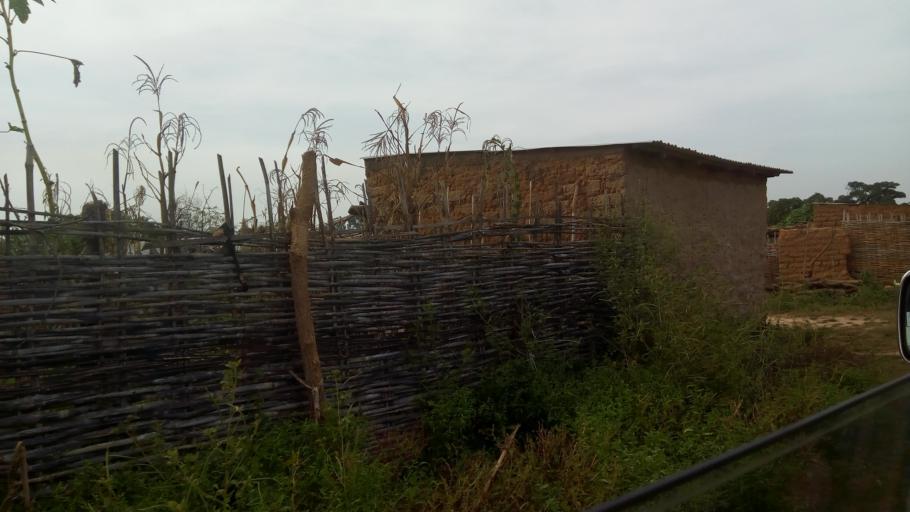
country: ML
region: Kayes
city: Kita
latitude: 13.1607
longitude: -8.8895
